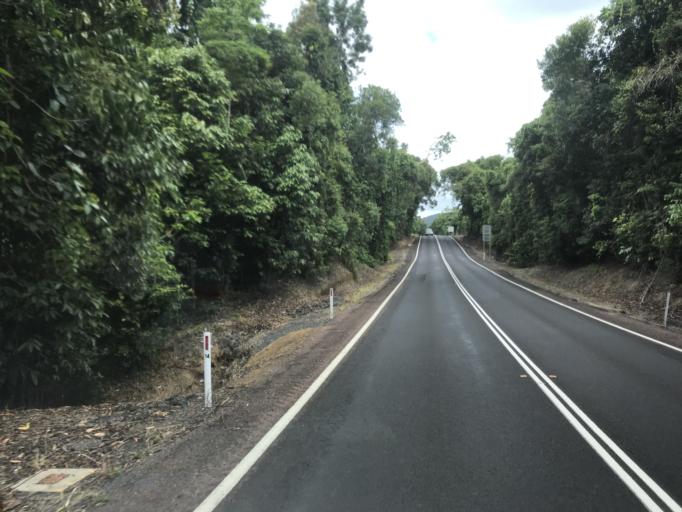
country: AU
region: Queensland
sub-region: Cassowary Coast
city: Innisfail
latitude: -17.8610
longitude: 146.0651
